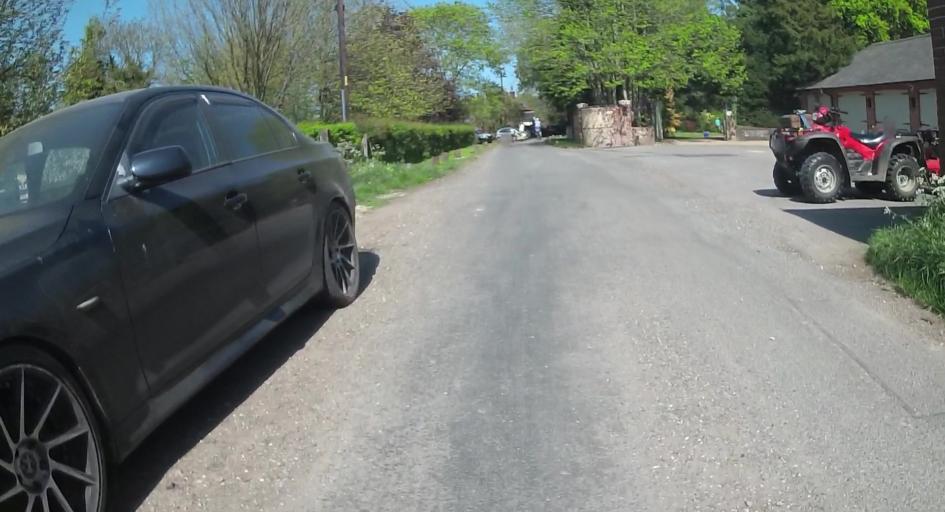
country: GB
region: England
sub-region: Hampshire
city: Four Marks
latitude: 51.1402
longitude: -1.0375
